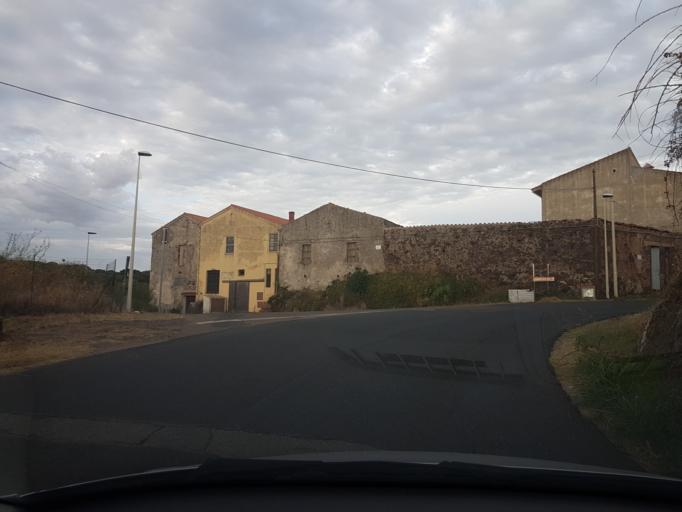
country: IT
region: Sardinia
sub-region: Provincia di Oristano
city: Seneghe
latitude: 40.0827
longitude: 8.6074
